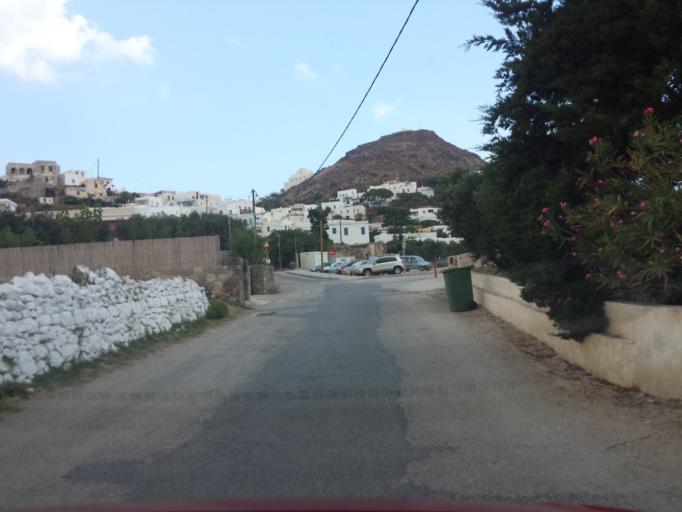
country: GR
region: South Aegean
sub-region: Nomos Kykladon
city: Milos
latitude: 36.7420
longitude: 24.4246
